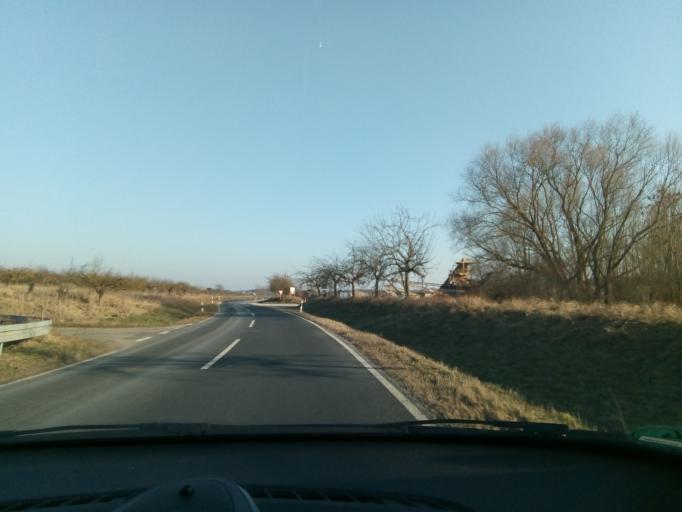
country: DE
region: Bavaria
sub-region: Regierungsbezirk Unterfranken
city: Nordheim
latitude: 49.8616
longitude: 10.2004
